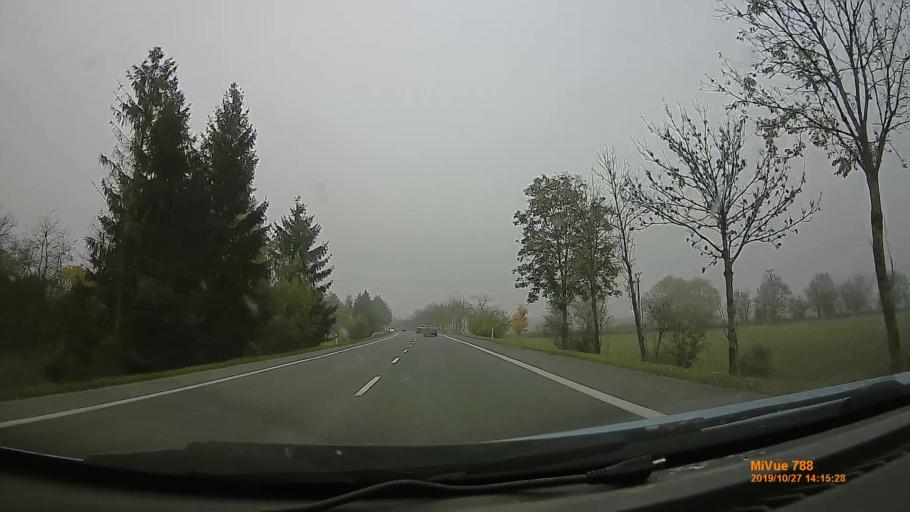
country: CZ
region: Olomoucky
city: Zabreh
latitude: 49.8806
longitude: 16.8933
